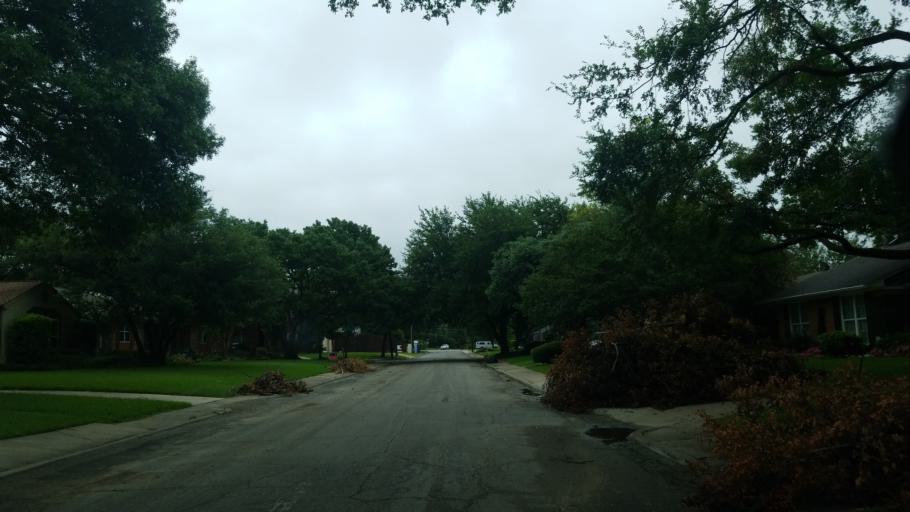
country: US
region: Texas
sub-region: Dallas County
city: Farmers Branch
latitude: 32.8924
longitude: -96.8582
